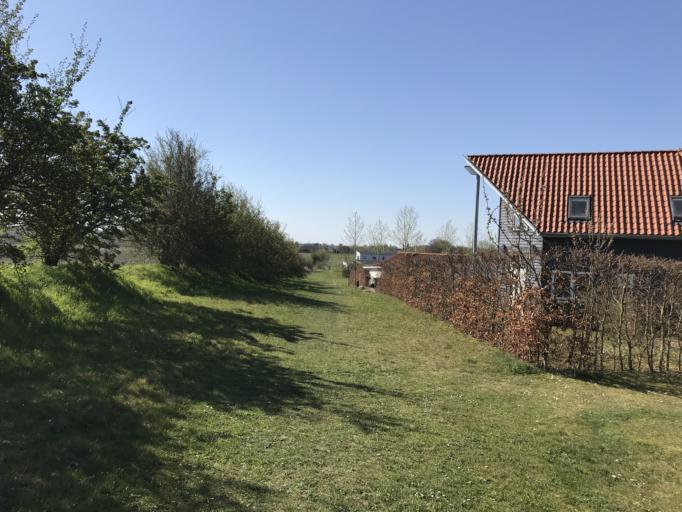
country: DK
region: Capital Region
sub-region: Hoje-Taastrup Kommune
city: Flong
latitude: 55.6606
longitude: 12.1530
